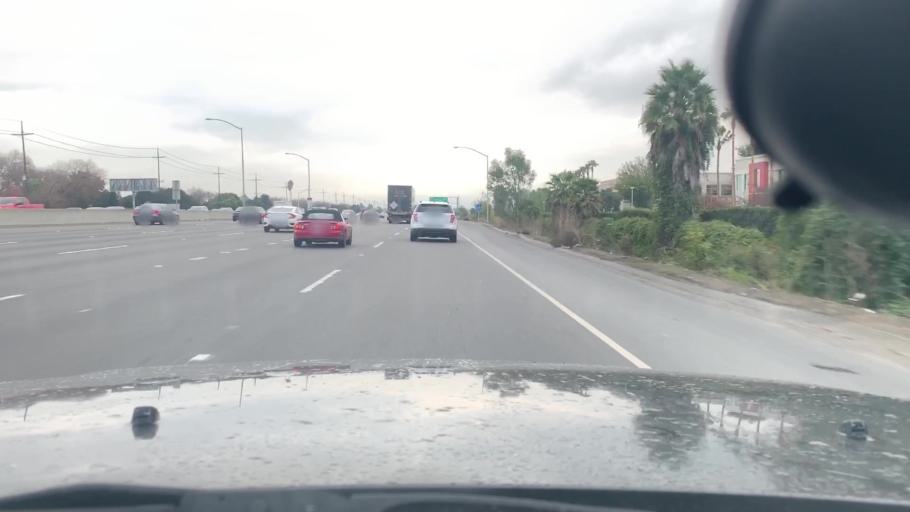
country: US
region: California
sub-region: Santa Clara County
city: Milpitas
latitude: 37.4408
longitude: -121.9205
